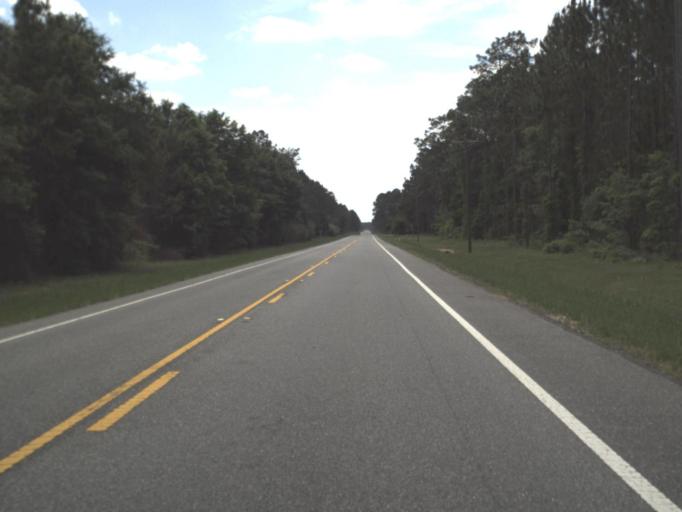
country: US
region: Florida
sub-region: Calhoun County
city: Blountstown
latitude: 30.3687
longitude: -85.0963
